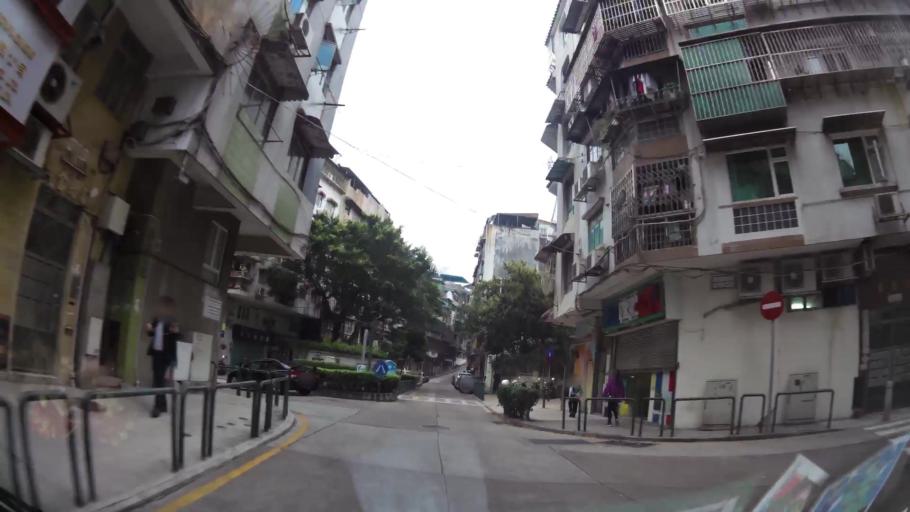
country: MO
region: Macau
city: Macau
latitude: 22.1974
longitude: 113.5436
